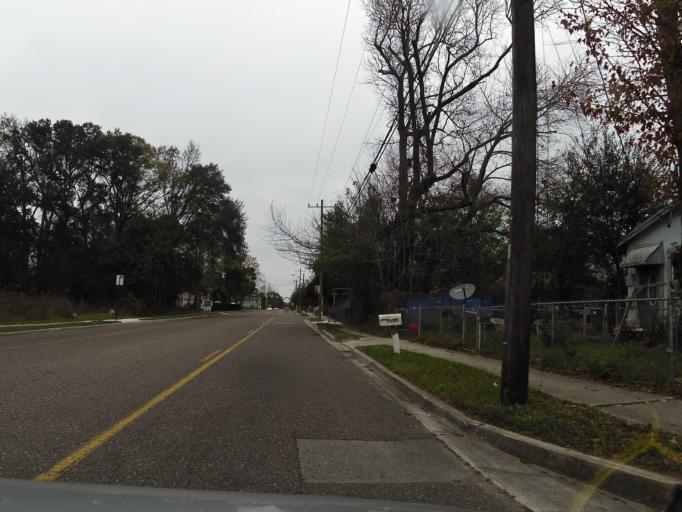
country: US
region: Florida
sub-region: Duval County
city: Jacksonville
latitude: 30.3693
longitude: -81.6989
